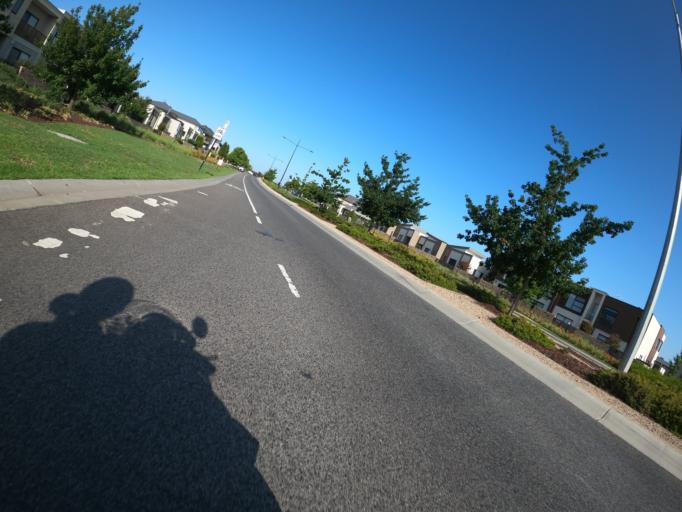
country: AU
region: Victoria
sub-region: Hume
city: Greenvale
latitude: -37.6137
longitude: 144.8881
